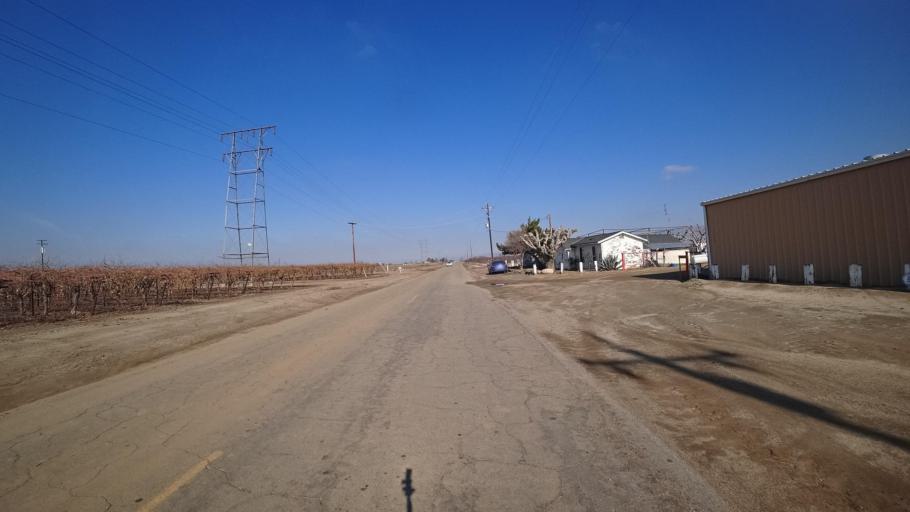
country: US
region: California
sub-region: Kern County
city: Arvin
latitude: 35.2010
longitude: -118.8065
